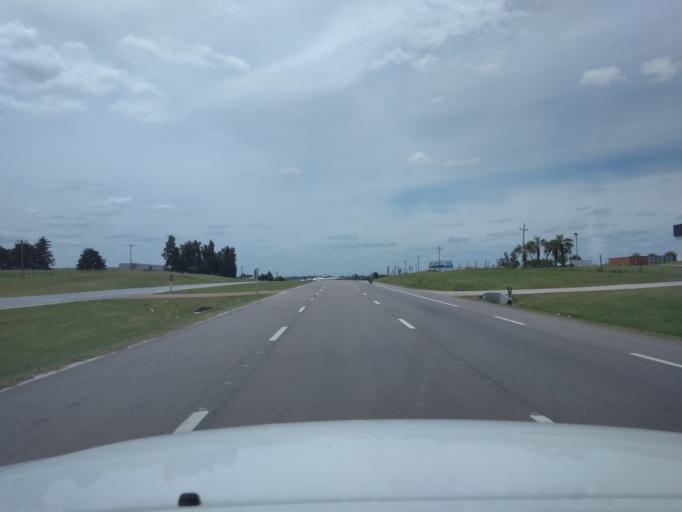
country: UY
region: Canelones
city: Las Piedras
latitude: -34.7050
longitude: -56.2409
